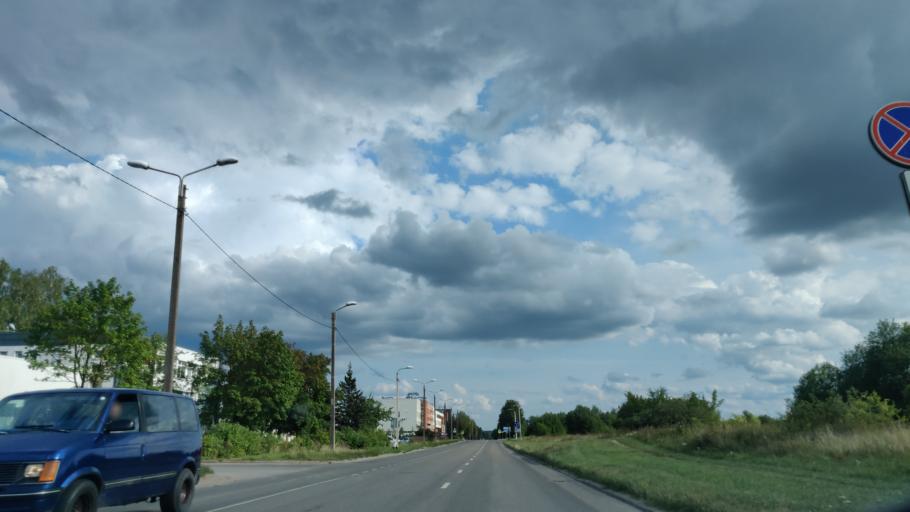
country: LT
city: Baltoji Voke
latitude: 54.6272
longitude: 25.1388
